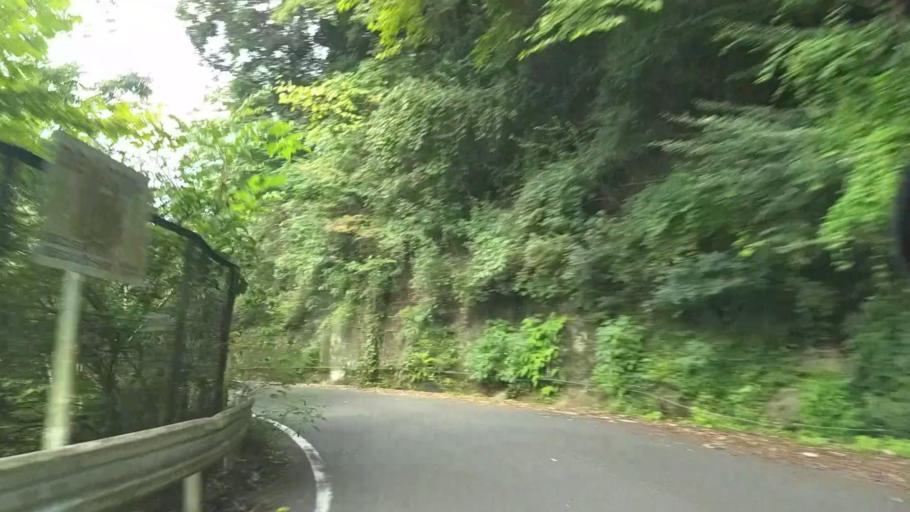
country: JP
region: Shizuoka
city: Fujinomiya
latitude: 35.2151
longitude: 138.5262
